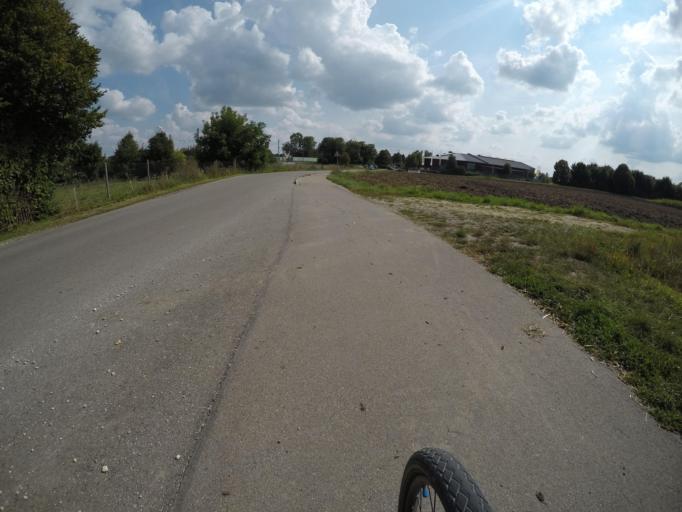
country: DE
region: Bavaria
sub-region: Swabia
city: Meitingen
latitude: 48.5499
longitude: 10.8467
